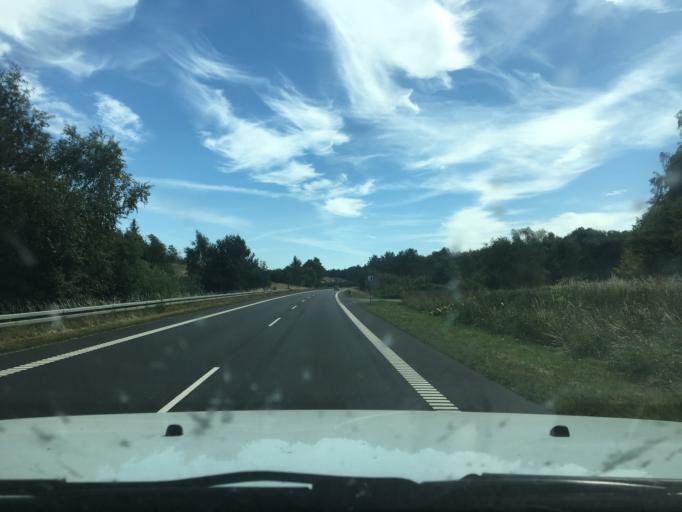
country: DK
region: Central Jutland
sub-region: Viborg Kommune
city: Viborg
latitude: 56.5214
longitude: 9.4043
